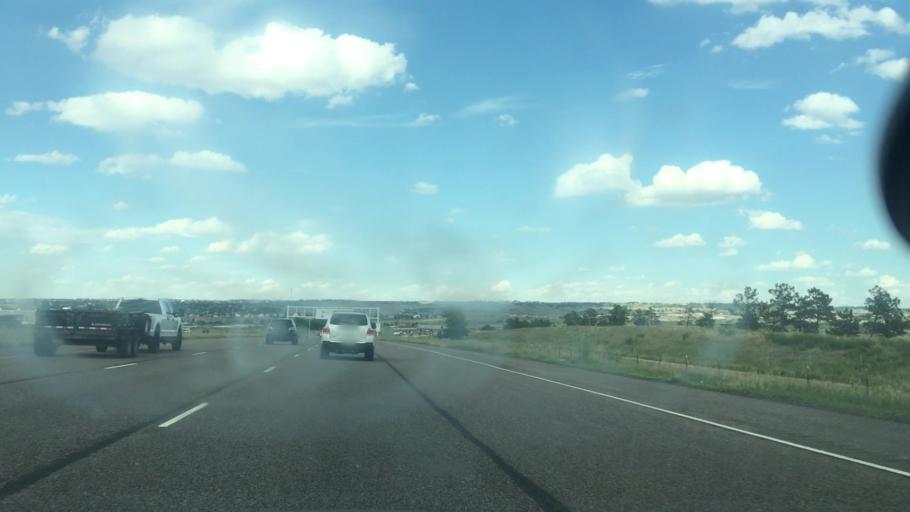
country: US
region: Colorado
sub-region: Arapahoe County
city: Dove Valley
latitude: 39.5541
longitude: -104.8316
